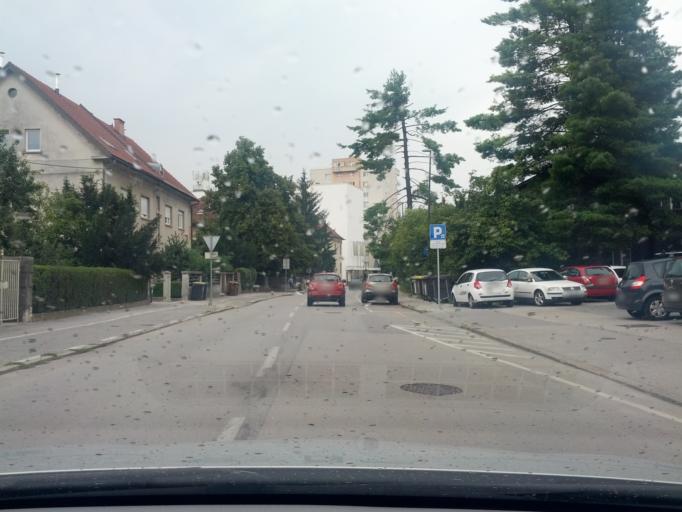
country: SI
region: Ljubljana
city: Ljubljana
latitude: 46.0634
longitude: 14.5040
